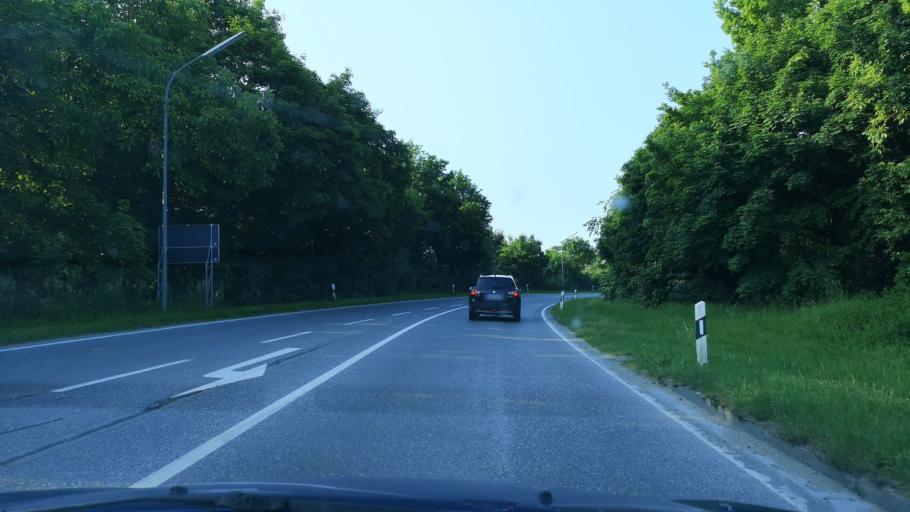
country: DE
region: Bavaria
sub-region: Upper Bavaria
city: Kirchheim bei Muenchen
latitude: 48.1754
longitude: 11.7649
